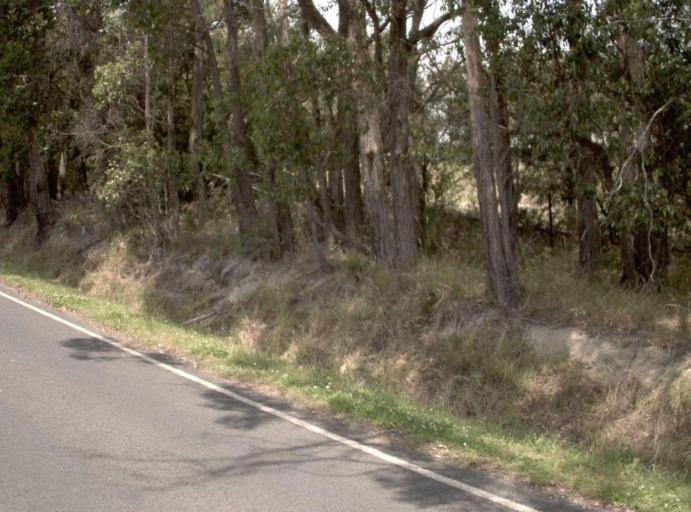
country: AU
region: Victoria
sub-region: Latrobe
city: Traralgon
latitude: -38.2562
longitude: 146.6766
